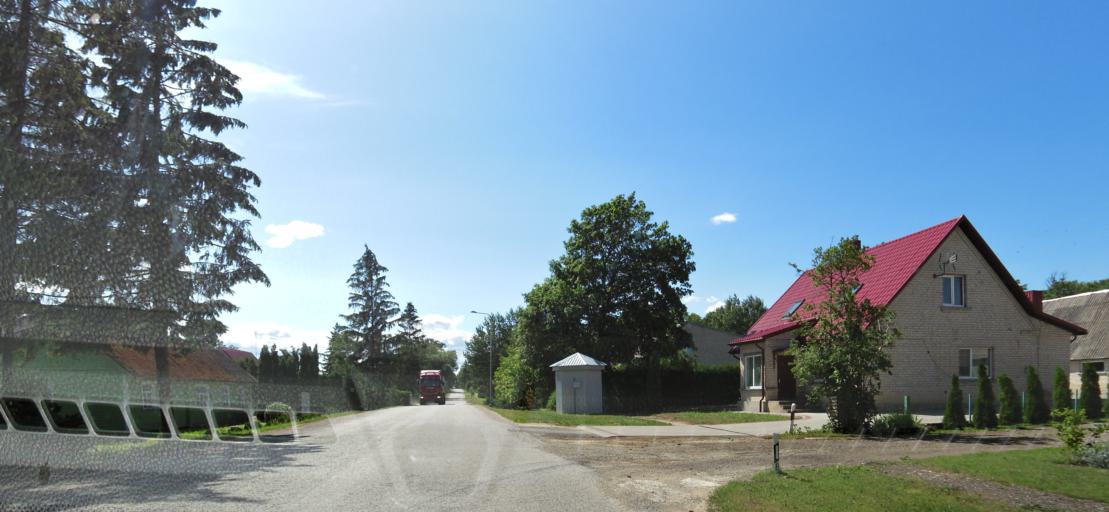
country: LV
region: Bauskas Rajons
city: Bauska
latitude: 56.2510
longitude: 24.2946
